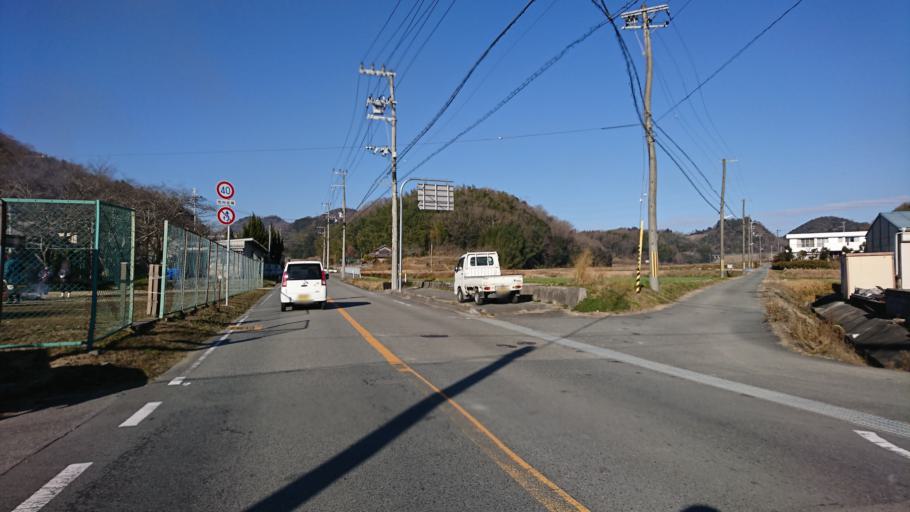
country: JP
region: Hyogo
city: Ono
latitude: 34.8418
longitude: 134.8619
